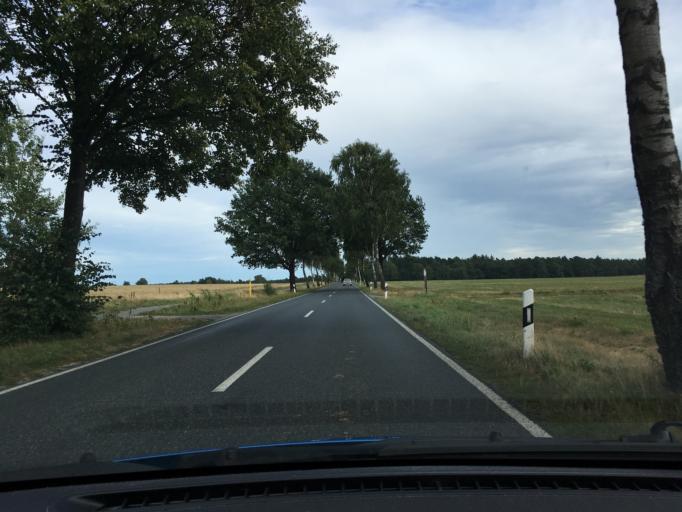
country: DE
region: Lower Saxony
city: Undeloh
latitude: 53.1971
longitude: 10.0028
